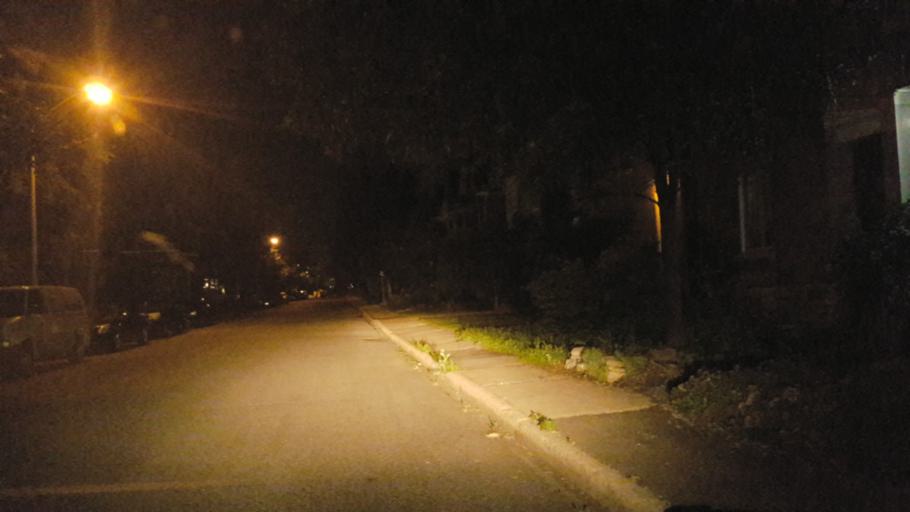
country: CA
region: Ontario
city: Ottawa
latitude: 45.4028
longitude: -75.7198
